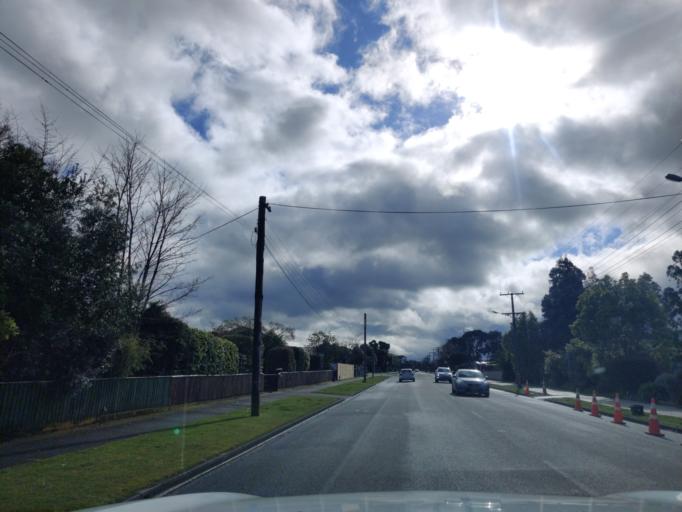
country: NZ
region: Manawatu-Wanganui
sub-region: Palmerston North City
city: Palmerston North
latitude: -40.2847
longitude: 175.7596
